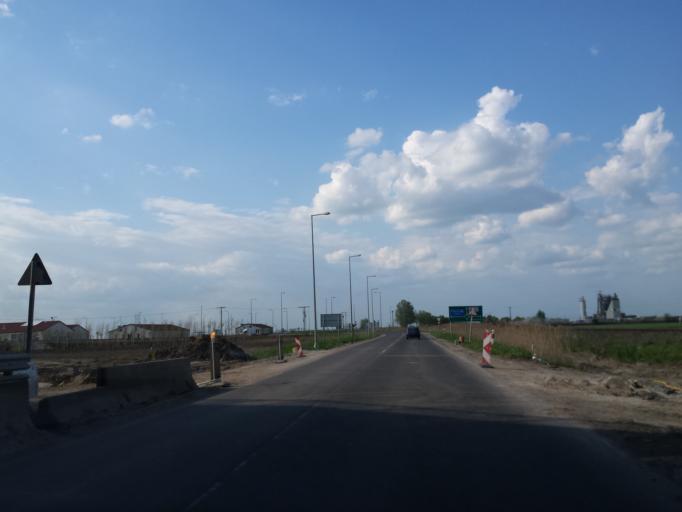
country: HU
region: Csongrad
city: Mako
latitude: 46.2678
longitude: 20.4816
